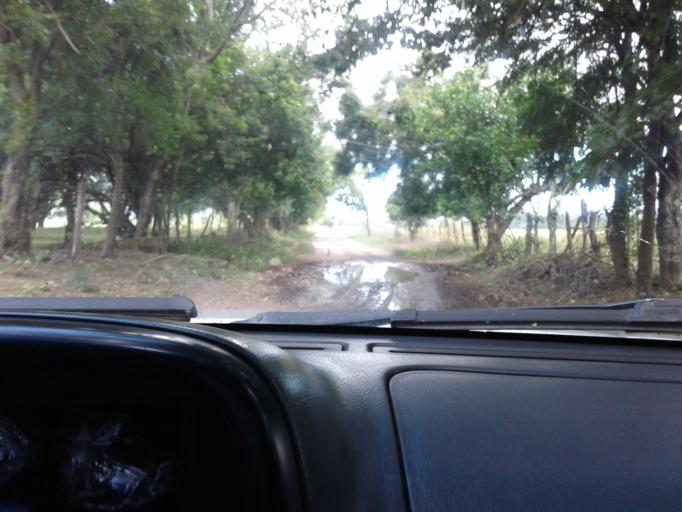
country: NI
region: Matagalpa
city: Ciudad Dario
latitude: 12.8494
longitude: -86.1331
